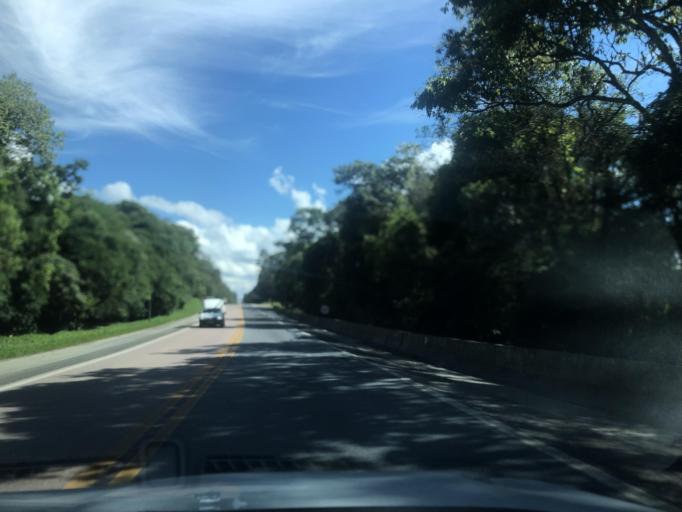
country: BR
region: Santa Catarina
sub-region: Canoinhas
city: Canoinhas
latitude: -26.3895
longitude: -50.2250
